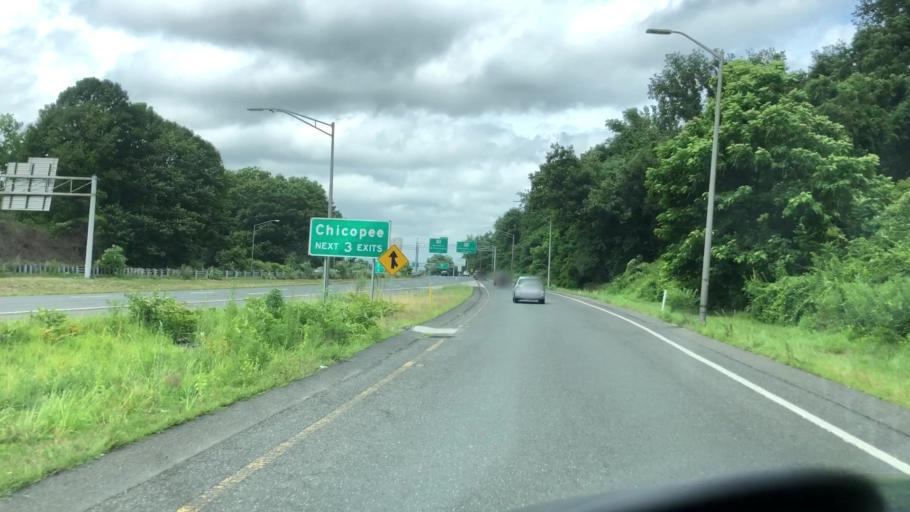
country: US
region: Massachusetts
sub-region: Hampden County
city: Chicopee
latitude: 42.1361
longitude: -72.6088
